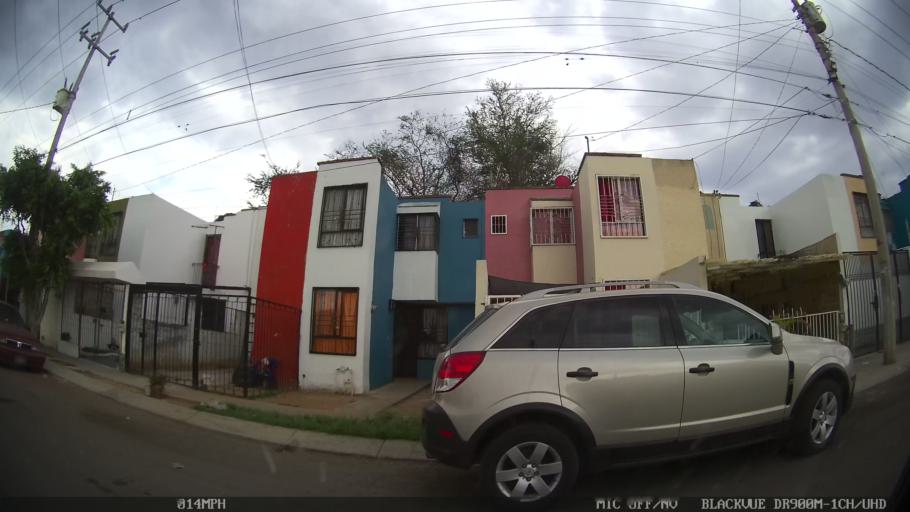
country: MX
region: Jalisco
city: Tlaquepaque
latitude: 20.6244
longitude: -103.2772
